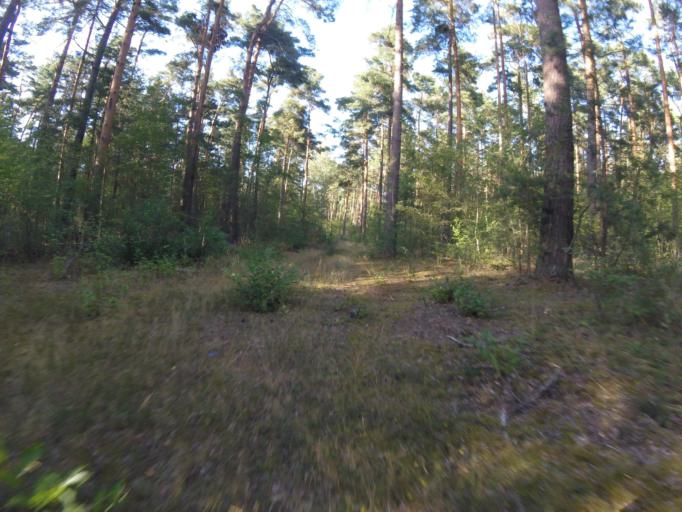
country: DE
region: Berlin
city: Schmockwitz
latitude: 52.3381
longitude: 13.6776
